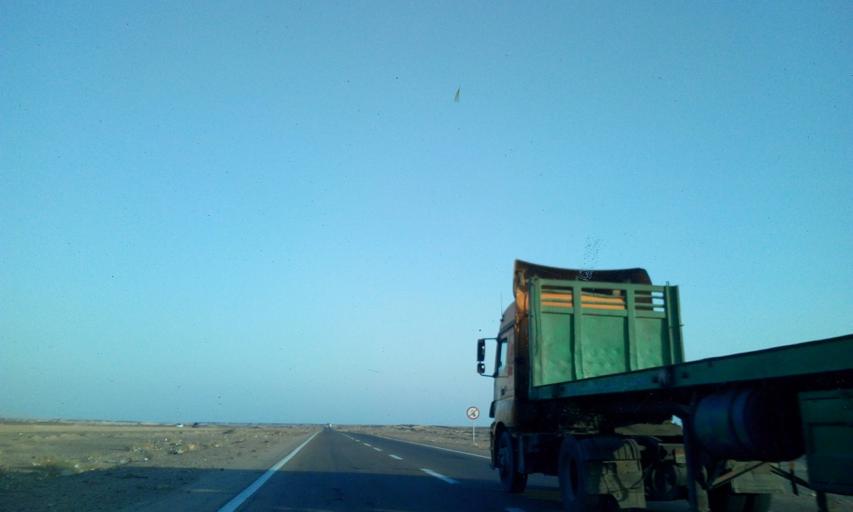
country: EG
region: South Sinai
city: Tor
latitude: 28.0150
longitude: 33.3103
